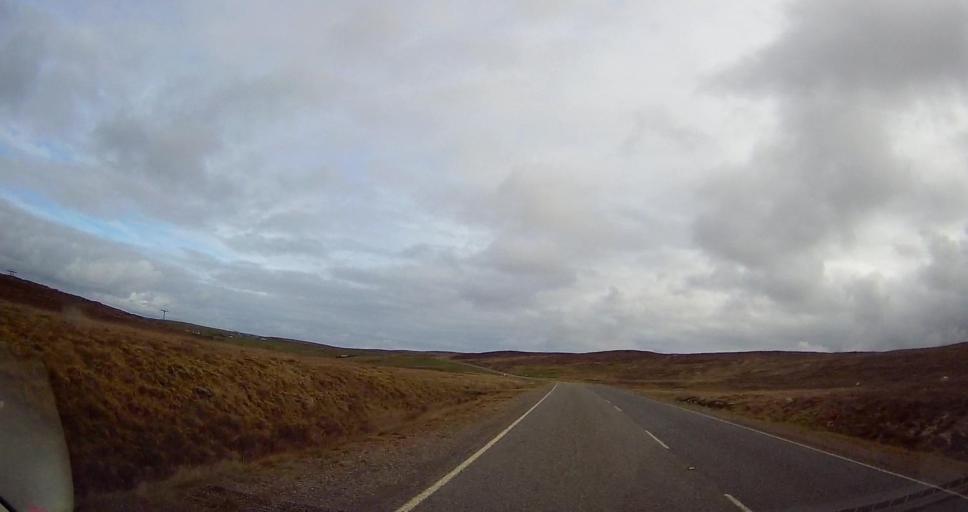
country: GB
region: Scotland
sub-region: Shetland Islands
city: Shetland
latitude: 60.5741
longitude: -1.1713
